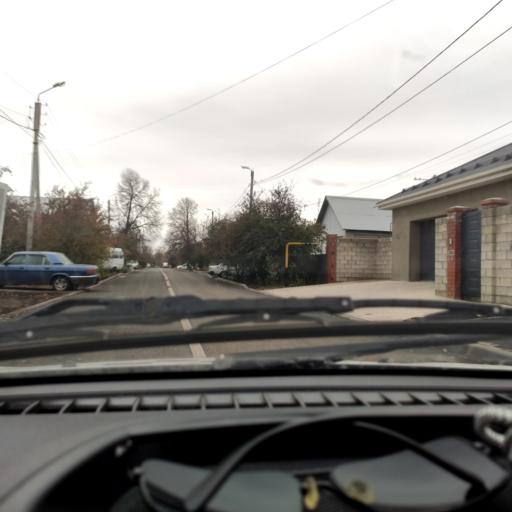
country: RU
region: Samara
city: Tol'yatti
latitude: 53.5287
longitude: 49.4236
